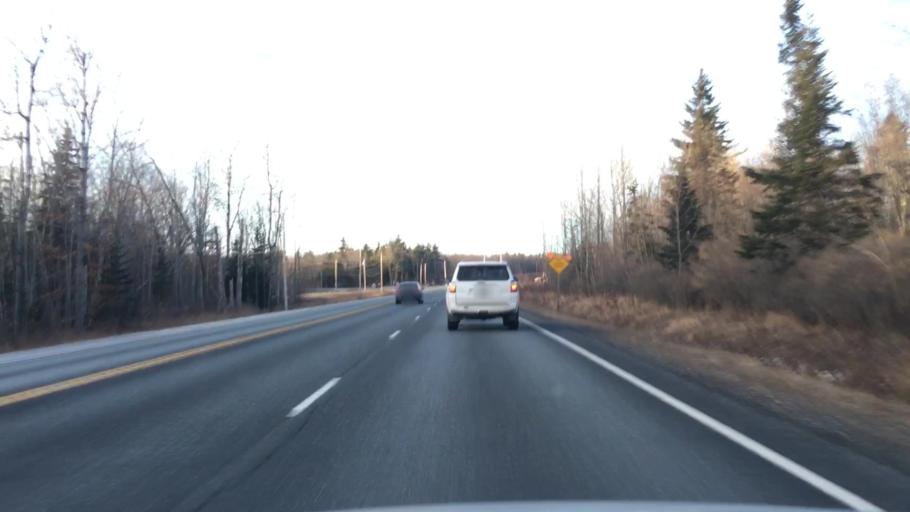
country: US
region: Maine
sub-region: Hancock County
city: Dedham
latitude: 44.6421
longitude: -68.5532
